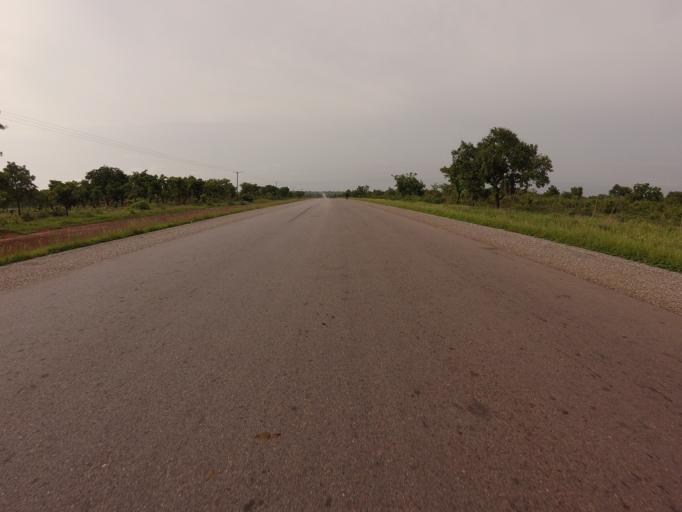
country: GH
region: Northern
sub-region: Yendi
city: Yendi
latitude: 9.6374
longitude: -0.0632
